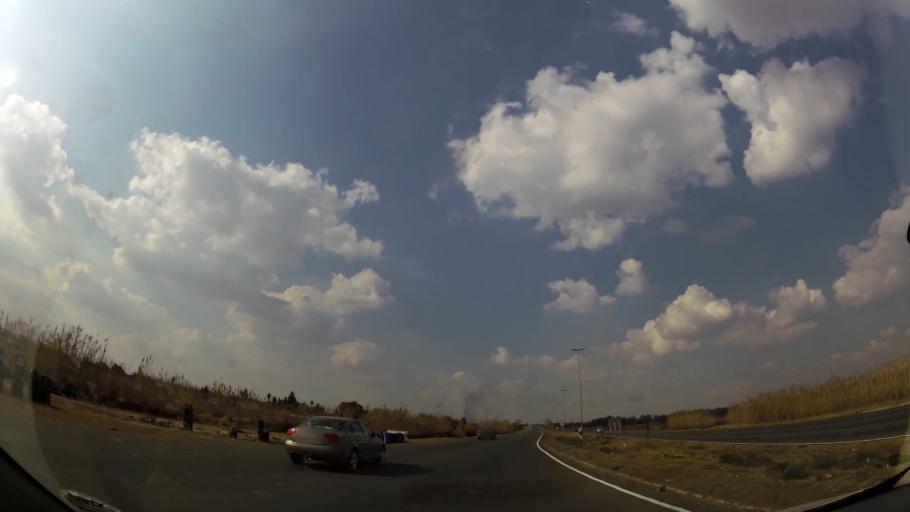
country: ZA
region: Gauteng
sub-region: Ekurhuleni Metropolitan Municipality
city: Germiston
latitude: -26.2944
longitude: 28.2121
